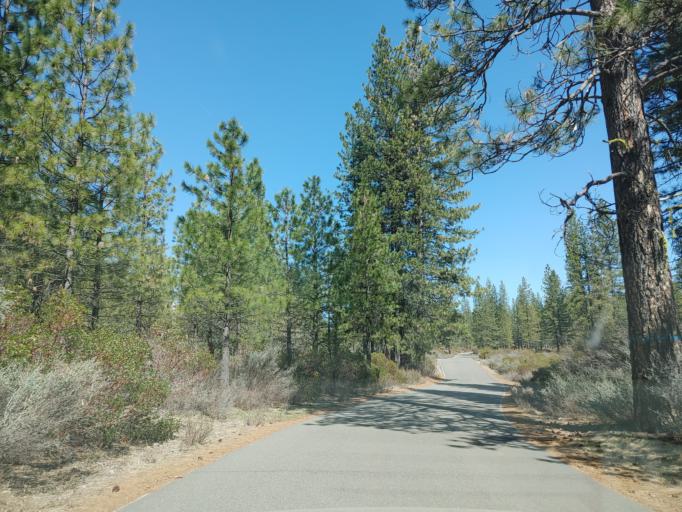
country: US
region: California
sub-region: Siskiyou County
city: McCloud
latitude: 41.2443
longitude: -122.0281
